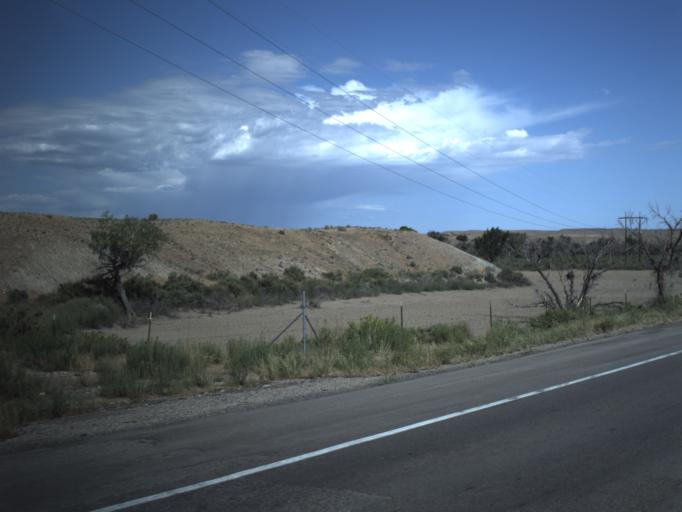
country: US
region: Utah
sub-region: Carbon County
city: East Carbon City
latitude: 39.2599
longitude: -110.3413
